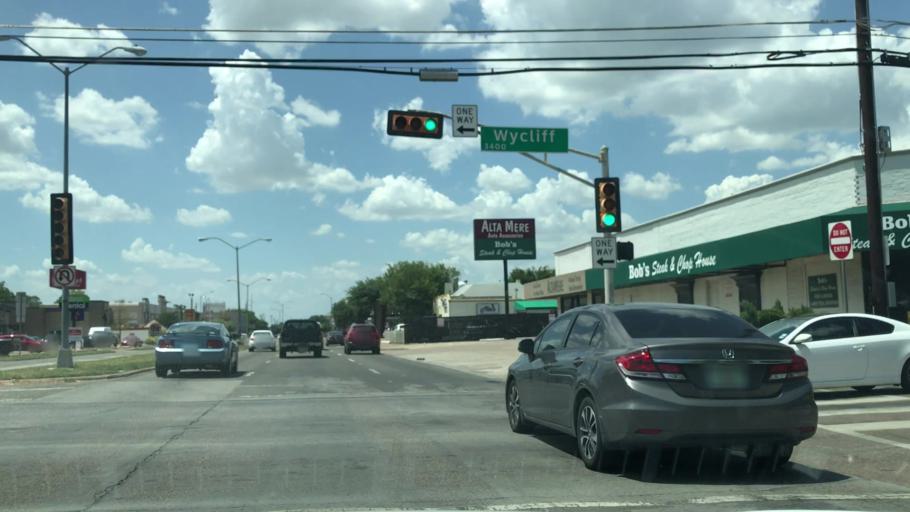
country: US
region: Texas
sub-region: Dallas County
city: Highland Park
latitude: 32.8169
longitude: -96.8112
